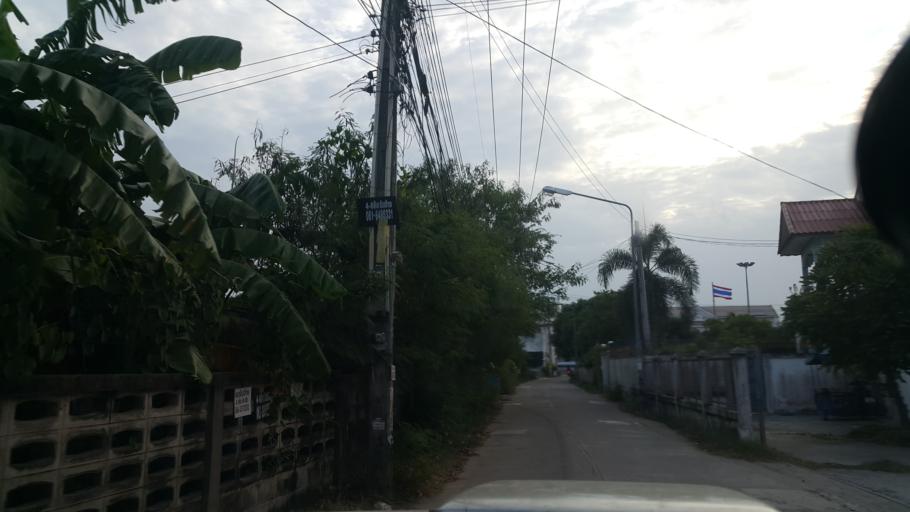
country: TH
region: Chon Buri
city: Phatthaya
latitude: 12.8181
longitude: 100.9180
